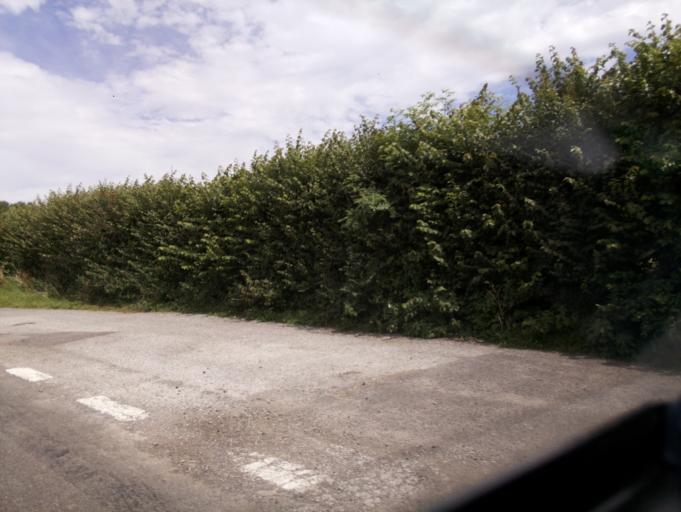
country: GB
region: England
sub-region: Somerset
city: Wells
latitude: 51.1949
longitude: -2.6680
